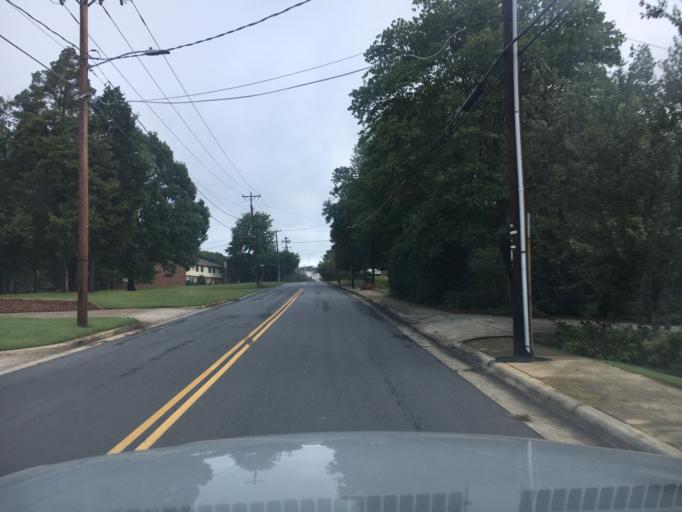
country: US
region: North Carolina
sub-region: Catawba County
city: Hickory
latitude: 35.7470
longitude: -81.3395
